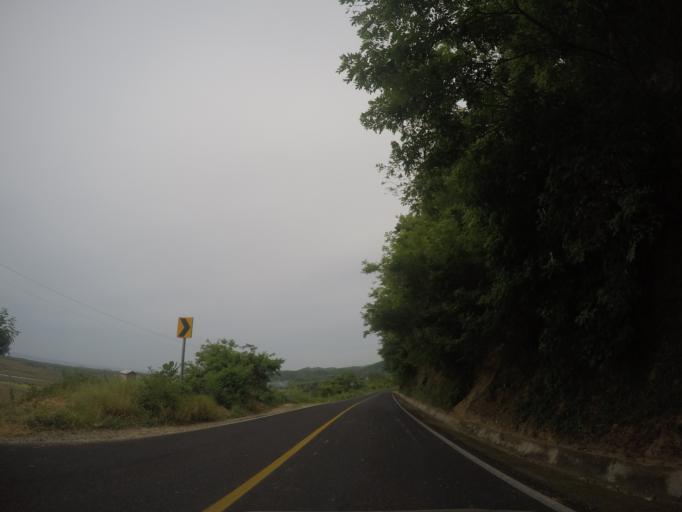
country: MX
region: Oaxaca
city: San Pedro Mixtepec
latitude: 15.9504
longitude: -97.2583
